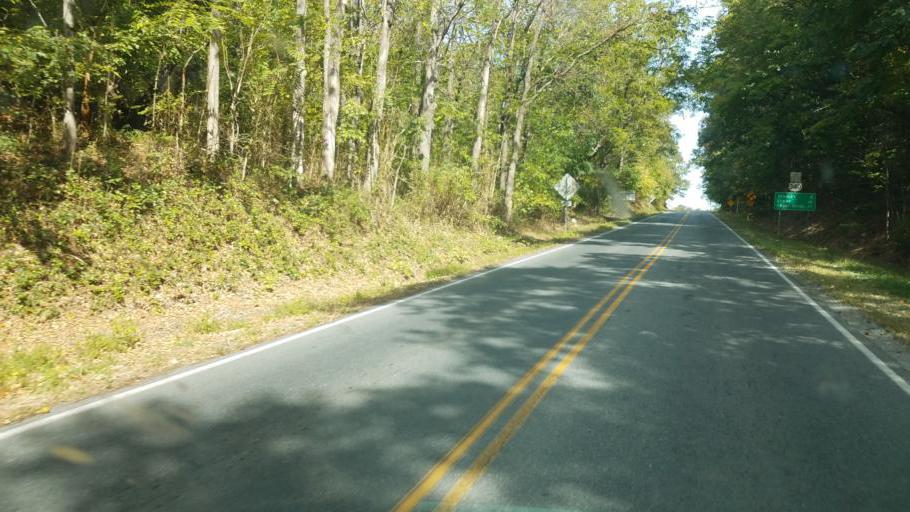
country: US
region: Virginia
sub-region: Page County
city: Stanley
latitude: 38.5895
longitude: -78.5906
